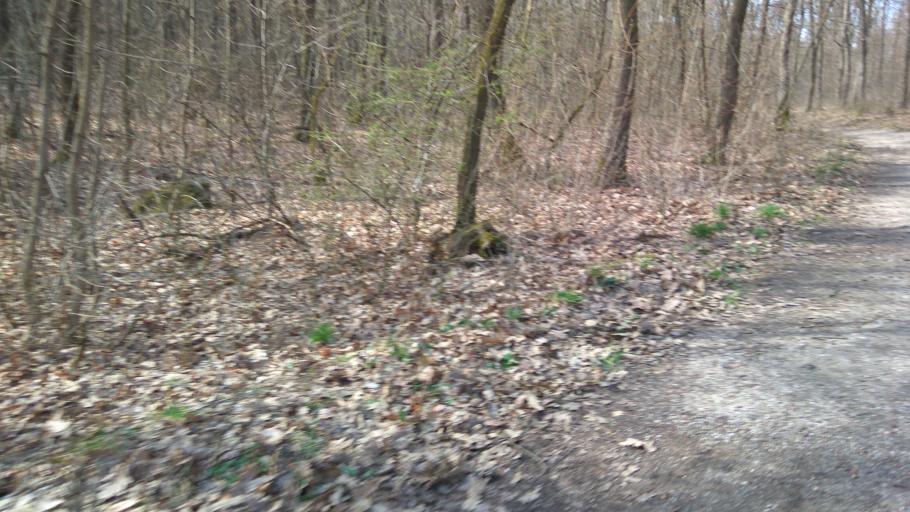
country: HU
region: Pest
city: Urom
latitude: 47.6154
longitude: 19.0114
